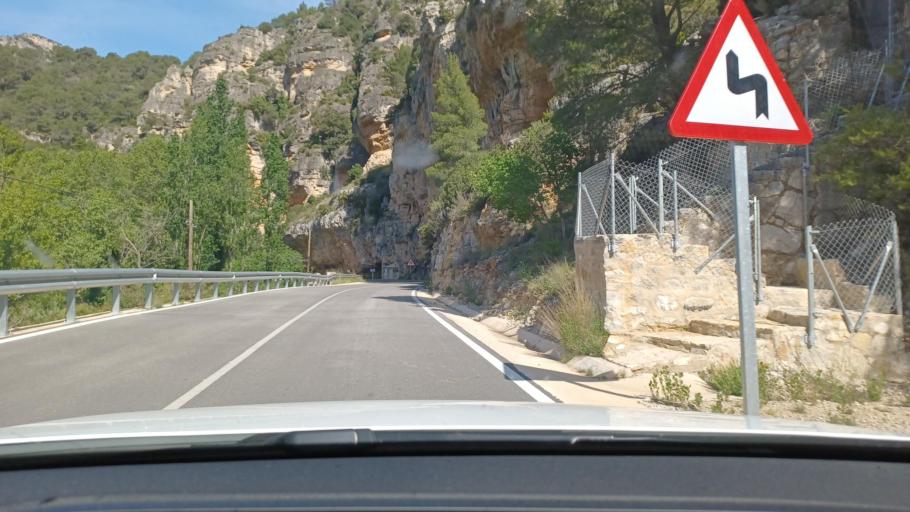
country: ES
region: Valencia
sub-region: Provincia de Castello
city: Rosell
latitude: 40.6716
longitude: 0.2393
